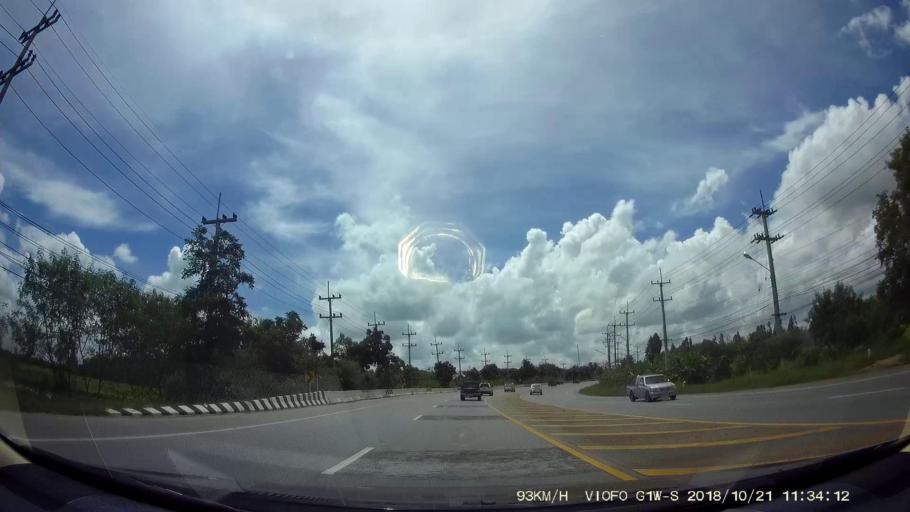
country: TH
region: Chaiyaphum
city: Chaiyaphum
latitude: 15.7347
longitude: 102.0244
